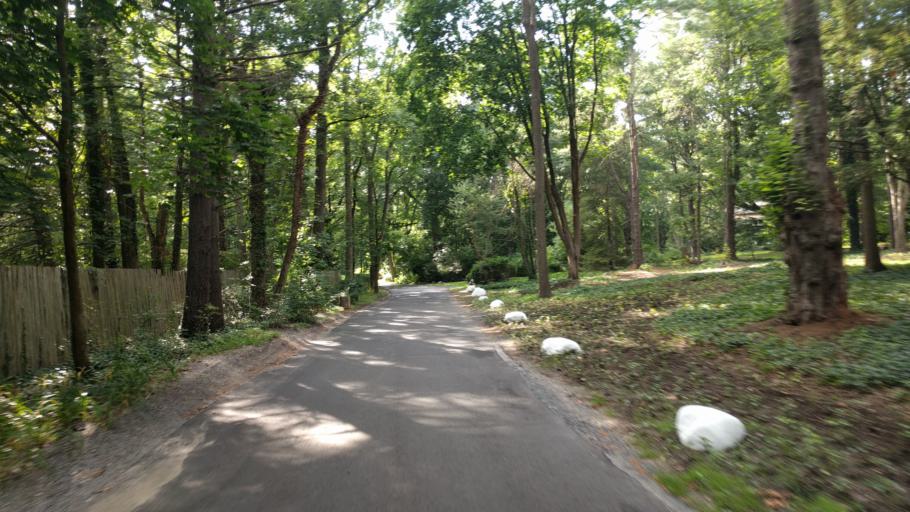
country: US
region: New York
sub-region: Nassau County
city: Oyster Bay Cove
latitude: 40.8696
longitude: -73.4988
